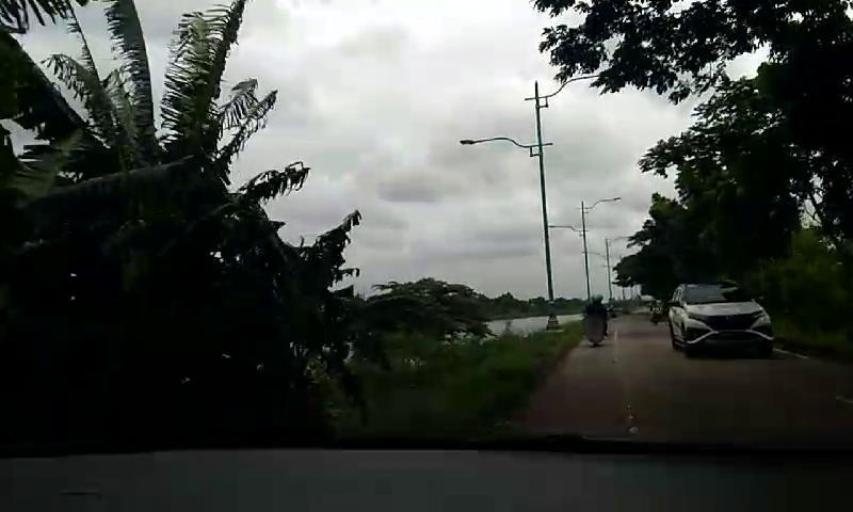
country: ID
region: West Java
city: Bekasi
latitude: -6.1260
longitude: 106.9692
